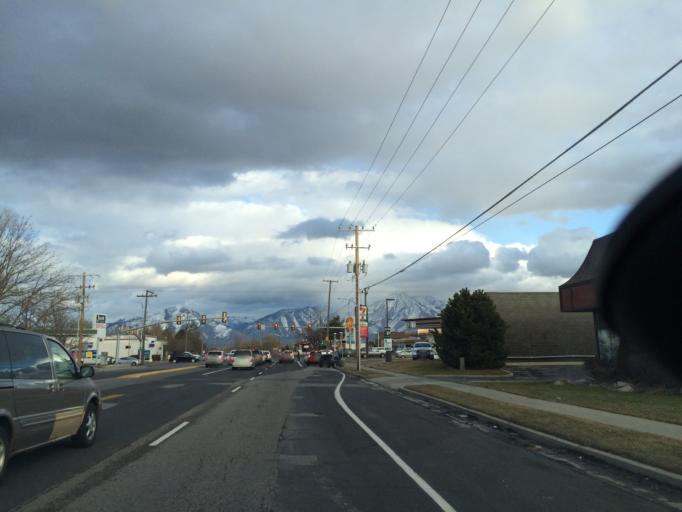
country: US
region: Utah
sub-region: Salt Lake County
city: Taylorsville
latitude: 40.6821
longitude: -111.9403
